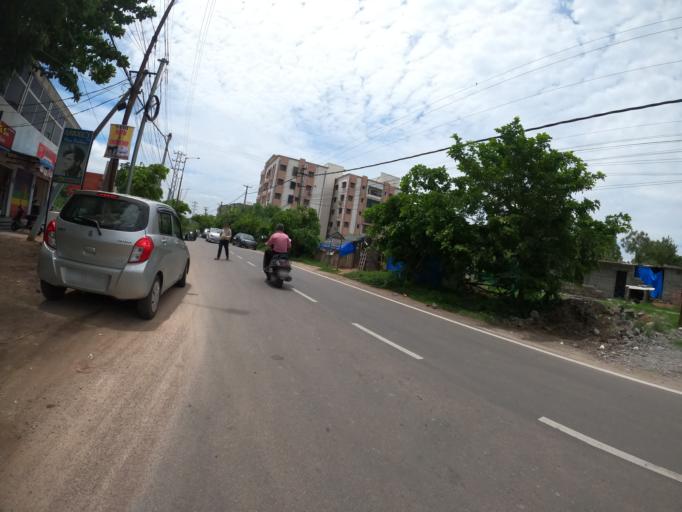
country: IN
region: Telangana
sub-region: Hyderabad
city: Hyderabad
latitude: 17.3658
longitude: 78.4157
